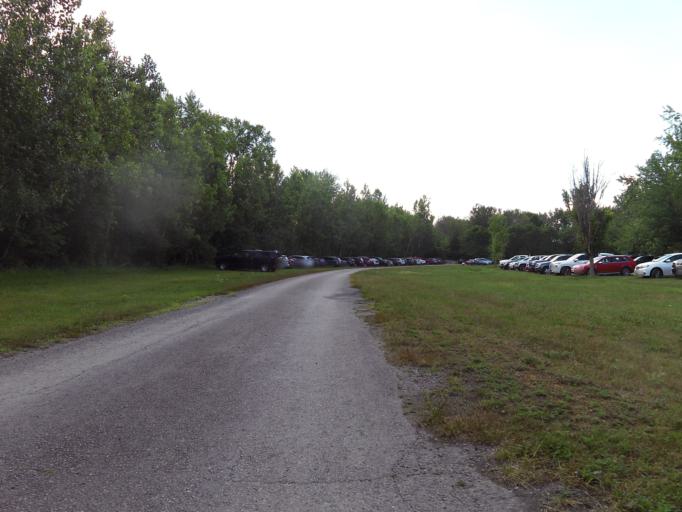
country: CA
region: Ontario
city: Arnprior
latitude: 45.4772
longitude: -76.2217
